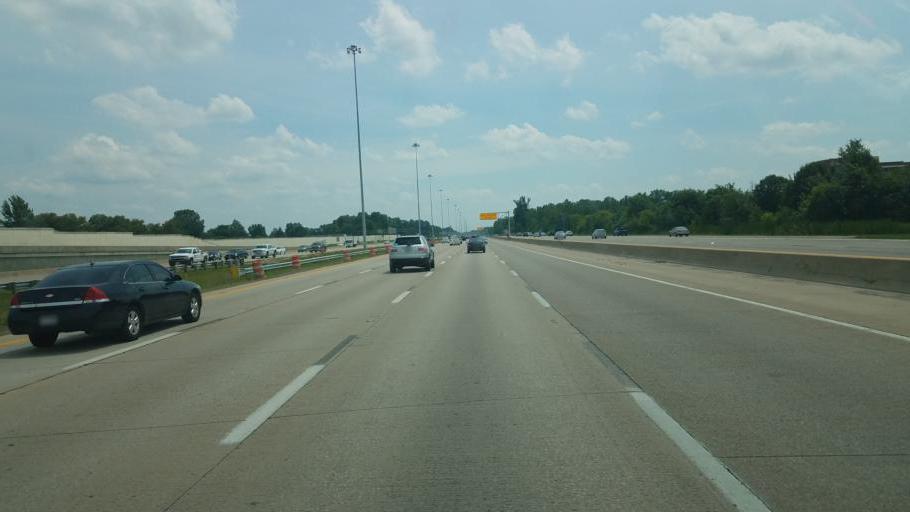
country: US
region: Ohio
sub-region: Franklin County
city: Gahanna
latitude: 40.0464
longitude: -82.9025
